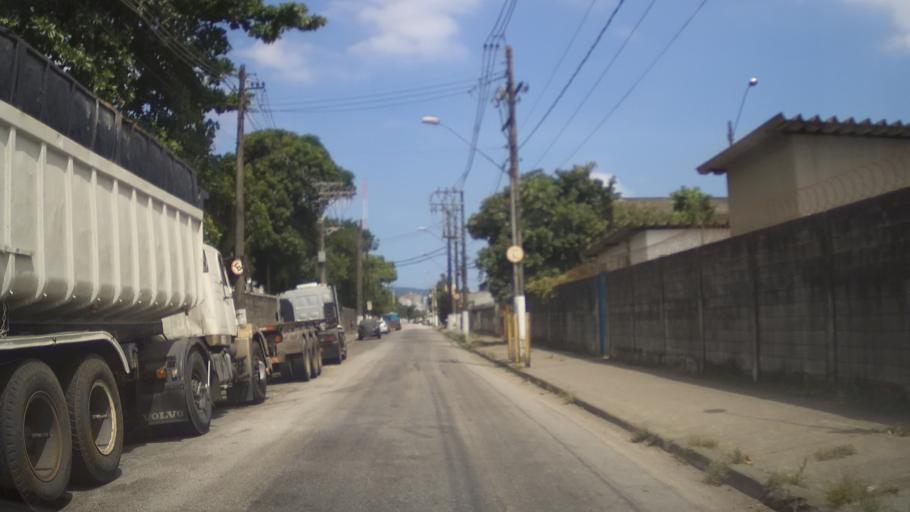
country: BR
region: Sao Paulo
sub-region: Santos
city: Santos
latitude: -23.9529
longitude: -46.3118
